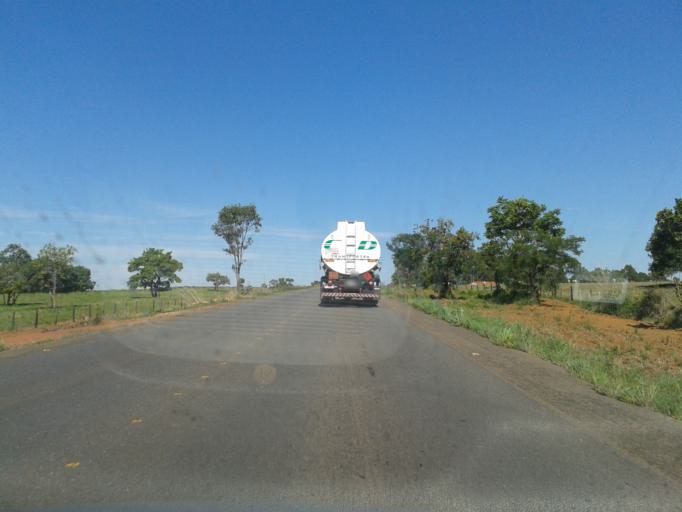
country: BR
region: Goias
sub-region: Bela Vista De Goias
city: Bela Vista de Goias
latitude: -17.0554
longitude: -48.9259
